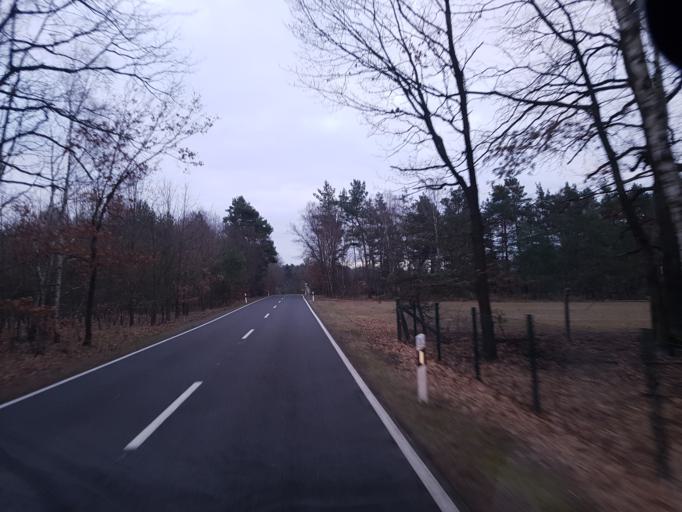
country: DE
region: Brandenburg
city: Sallgast
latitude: 51.5813
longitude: 13.8458
